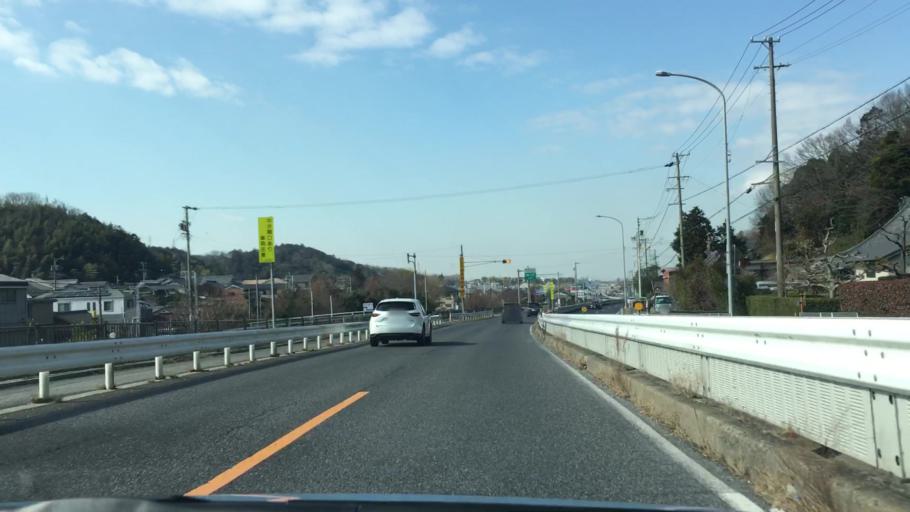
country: JP
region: Aichi
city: Okazaki
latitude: 34.9108
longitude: 137.2268
